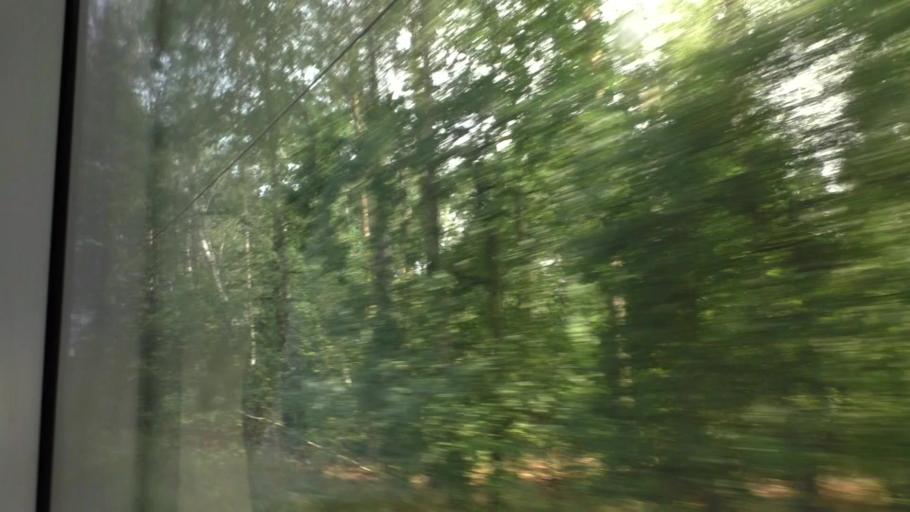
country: DE
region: Brandenburg
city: Bestensee
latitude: 52.2960
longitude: 13.7554
